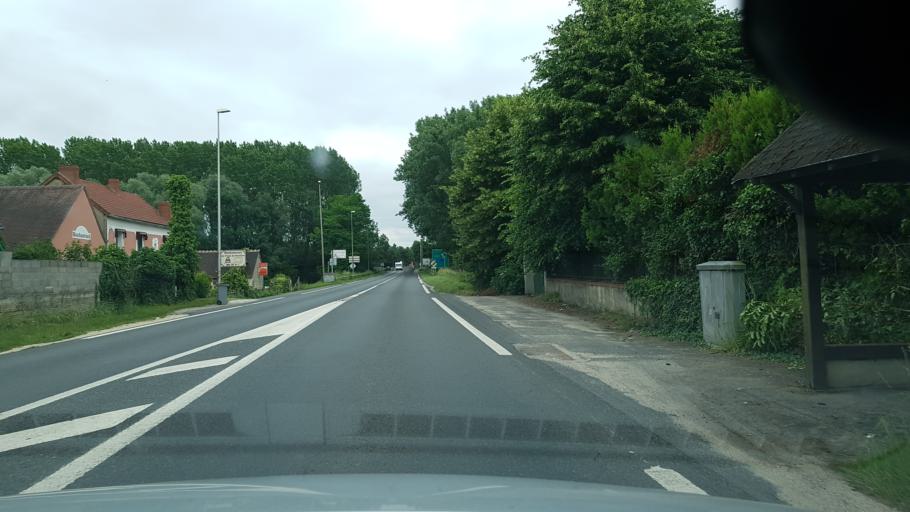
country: FR
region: Centre
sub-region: Departement du Loir-et-Cher
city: Selles-sur-Cher
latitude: 47.2885
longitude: 1.5331
